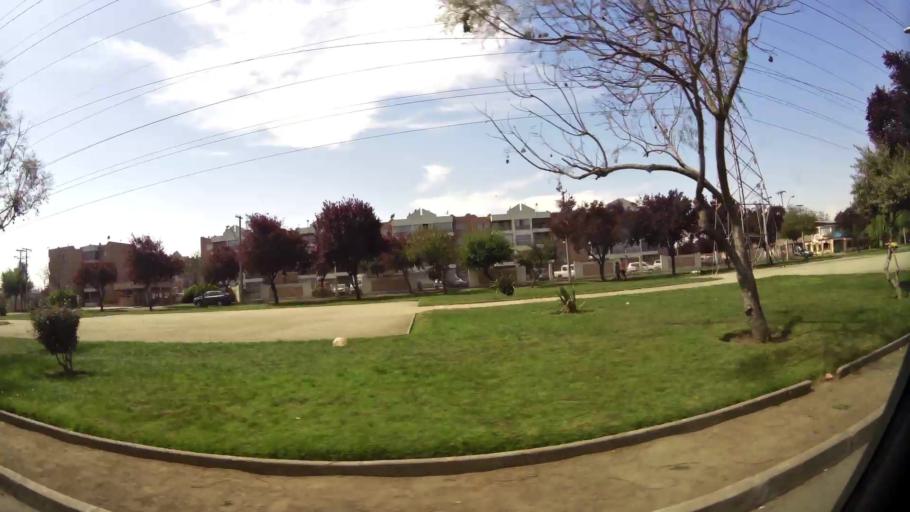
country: CL
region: Santiago Metropolitan
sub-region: Provincia de Santiago
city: Lo Prado
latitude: -33.4717
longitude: -70.7314
